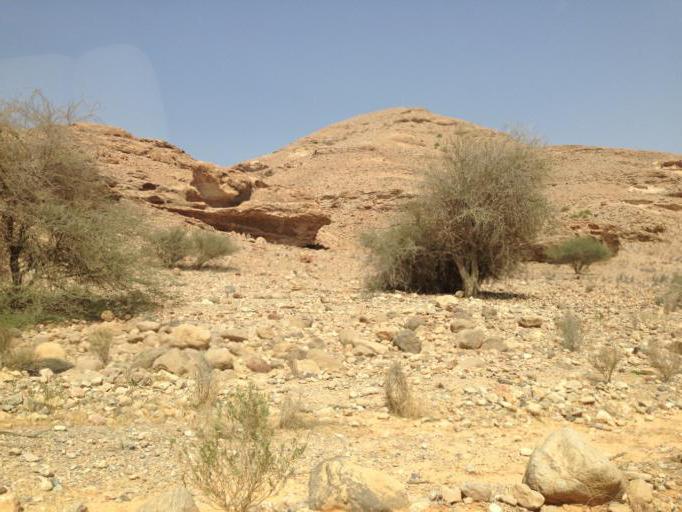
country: OM
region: Ash Sharqiyah
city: Ibra'
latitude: 23.0790
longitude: 58.8733
